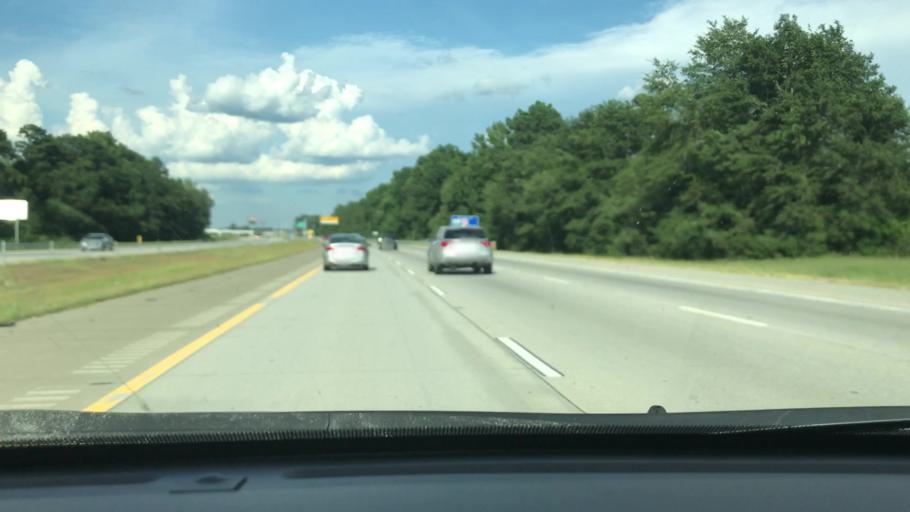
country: US
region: South Carolina
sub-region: Florence County
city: Florence
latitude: 34.2652
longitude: -79.7151
